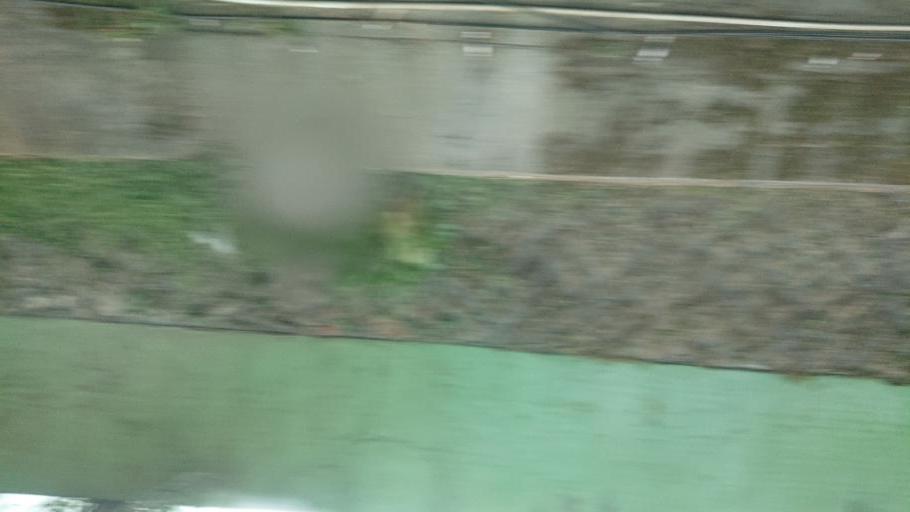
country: TW
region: Taiwan
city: Lugu
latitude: 23.6061
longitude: 120.7081
